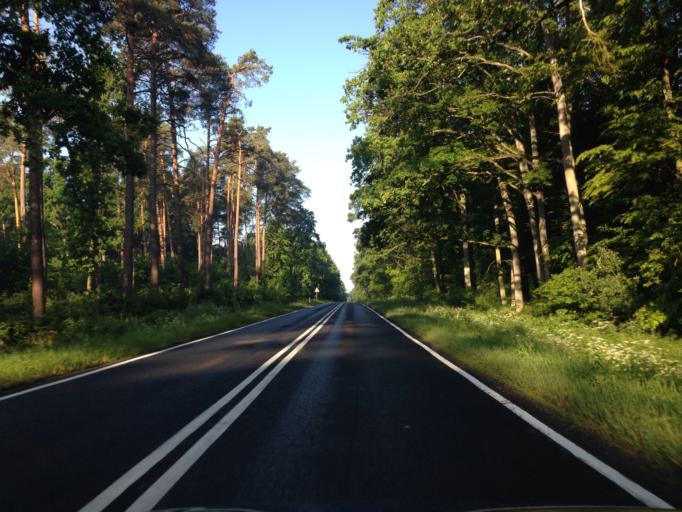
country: PL
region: Pomeranian Voivodeship
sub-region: Powiat kwidzynski
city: Gardeja
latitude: 53.5835
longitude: 18.9013
